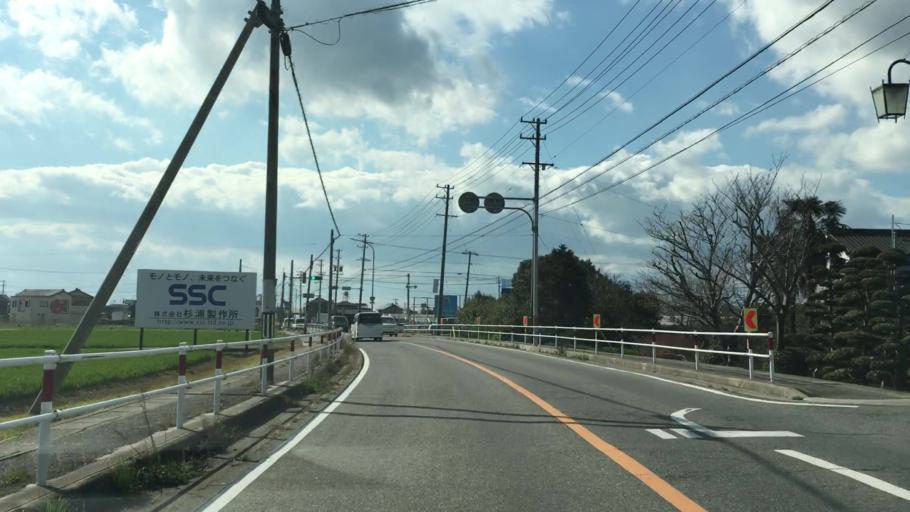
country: JP
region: Aichi
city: Ishiki
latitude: 34.7976
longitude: 137.0537
